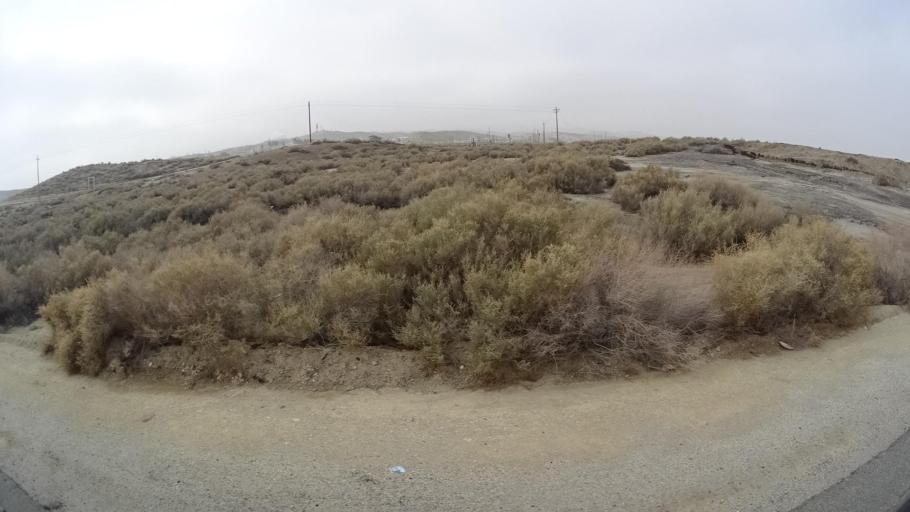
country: US
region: California
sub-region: Kern County
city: Maricopa
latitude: 35.0910
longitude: -119.4007
